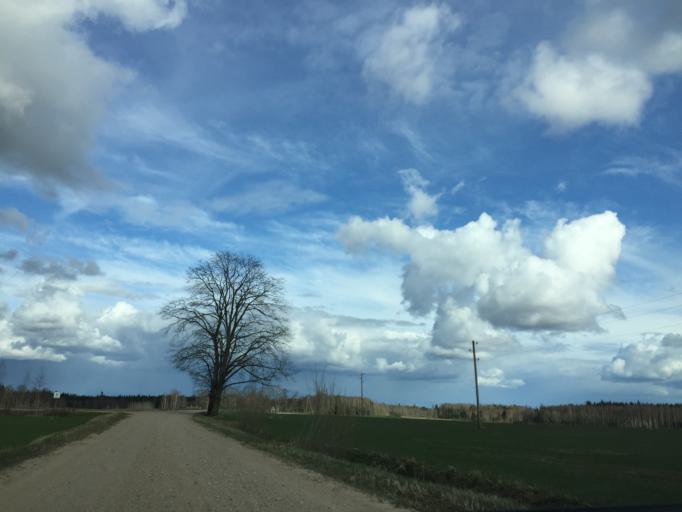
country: LV
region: Burtnieki
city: Matisi
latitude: 57.6117
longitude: 25.0248
